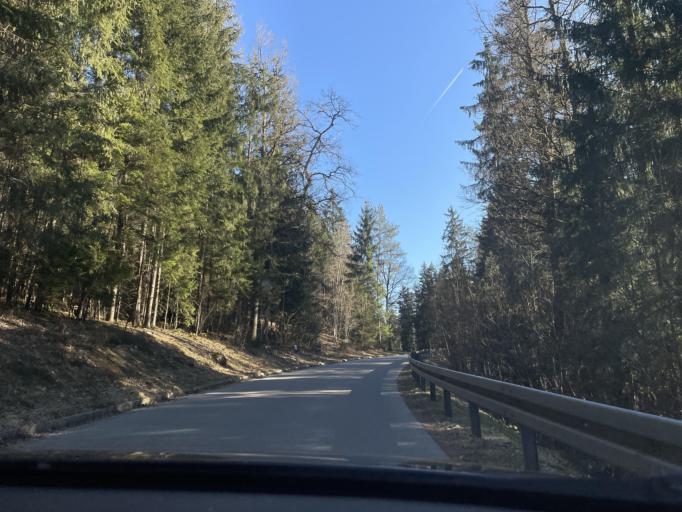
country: DE
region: Bavaria
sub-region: Lower Bavaria
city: Geiersthal
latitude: 49.0765
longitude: 12.9917
